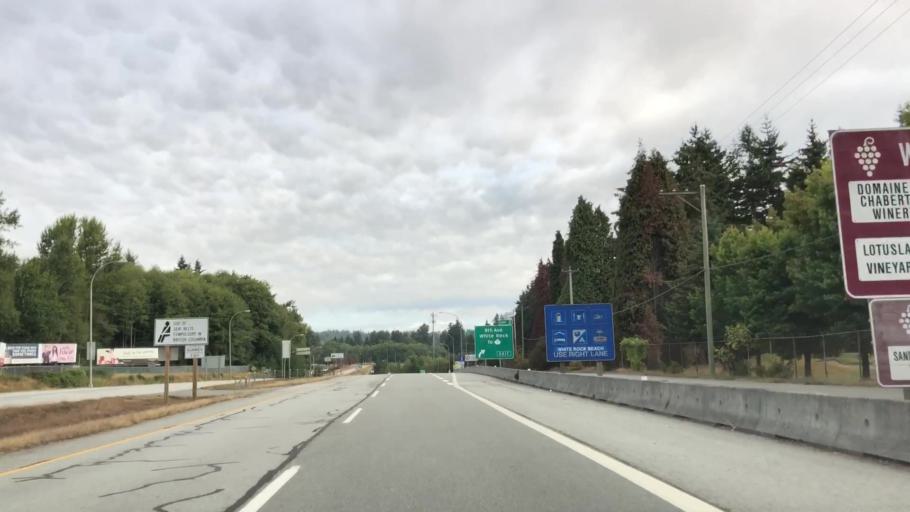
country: US
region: Washington
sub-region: Whatcom County
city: Blaine
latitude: 49.0097
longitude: -122.7574
